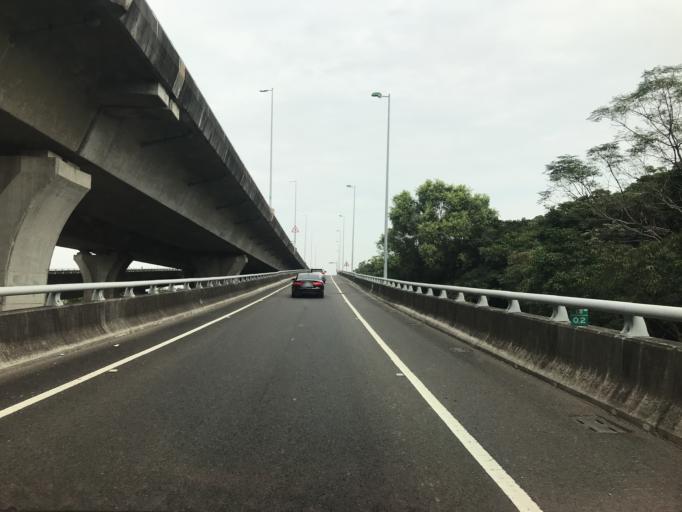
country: TW
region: Taiwan
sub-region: Pingtung
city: Pingtung
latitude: 22.6459
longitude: 120.5423
